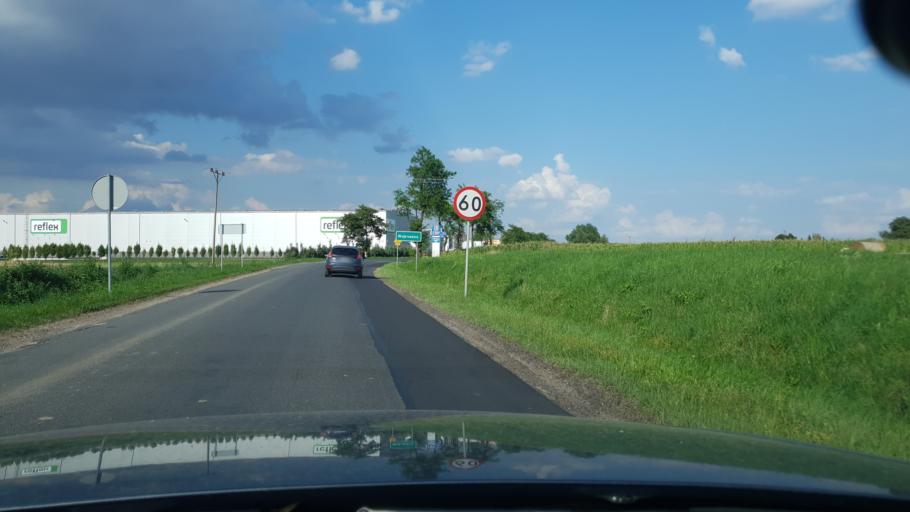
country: PL
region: Kujawsko-Pomorskie
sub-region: Powiat wabrzeski
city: Wabrzezno
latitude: 53.2732
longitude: 18.9186
